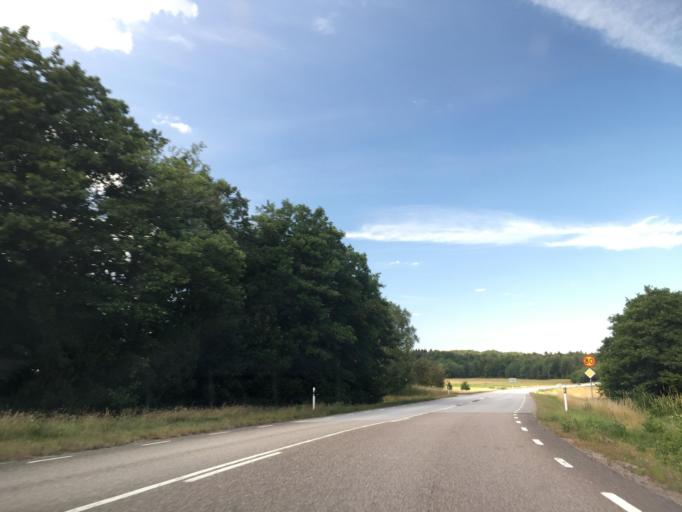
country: SE
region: Vaestra Goetaland
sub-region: Tanums Kommun
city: Tanumshede
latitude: 58.8115
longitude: 11.2640
